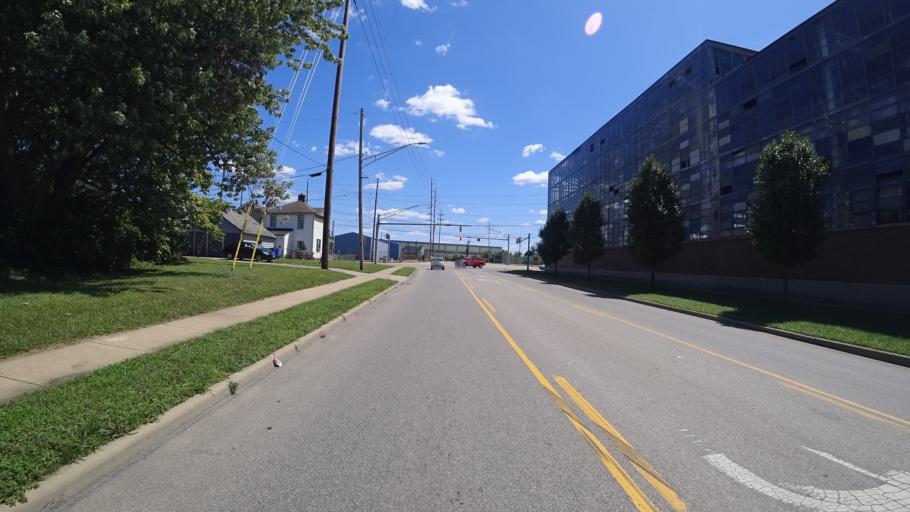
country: US
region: Ohio
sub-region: Butler County
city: Hamilton
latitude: 39.4086
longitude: -84.5566
